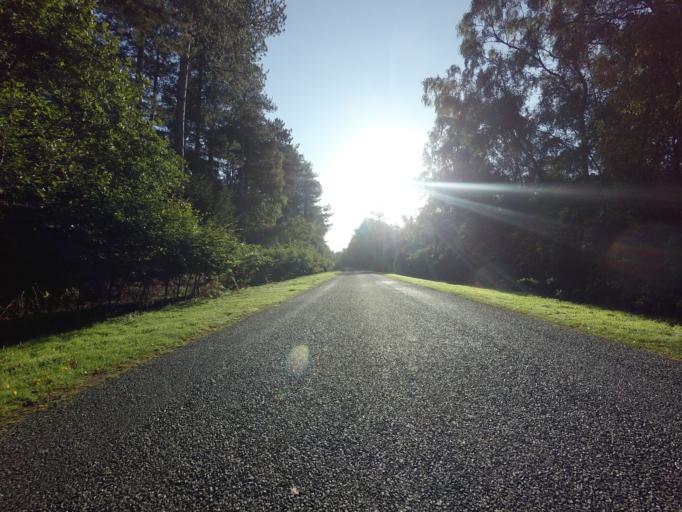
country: GB
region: England
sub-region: Norfolk
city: Dersingham
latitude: 52.8170
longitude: 0.4992
